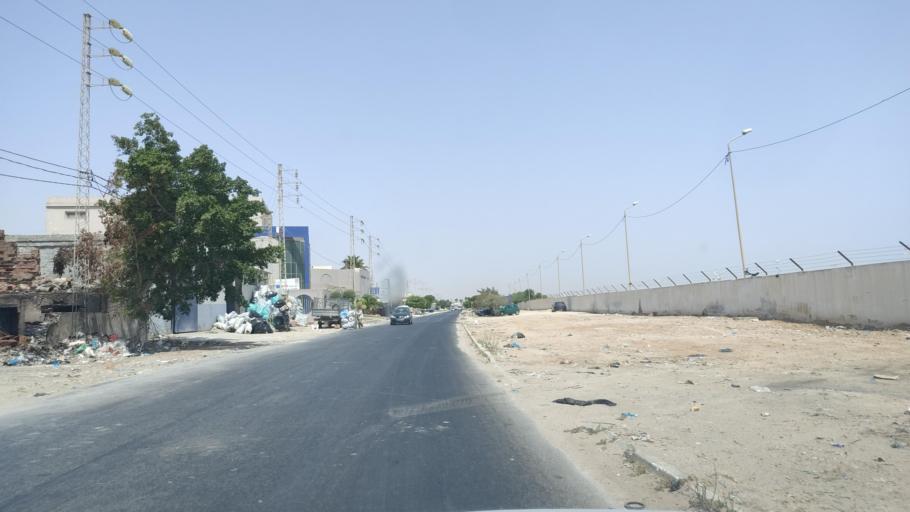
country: TN
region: Safaqis
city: Sfax
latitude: 34.6951
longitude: 10.7235
